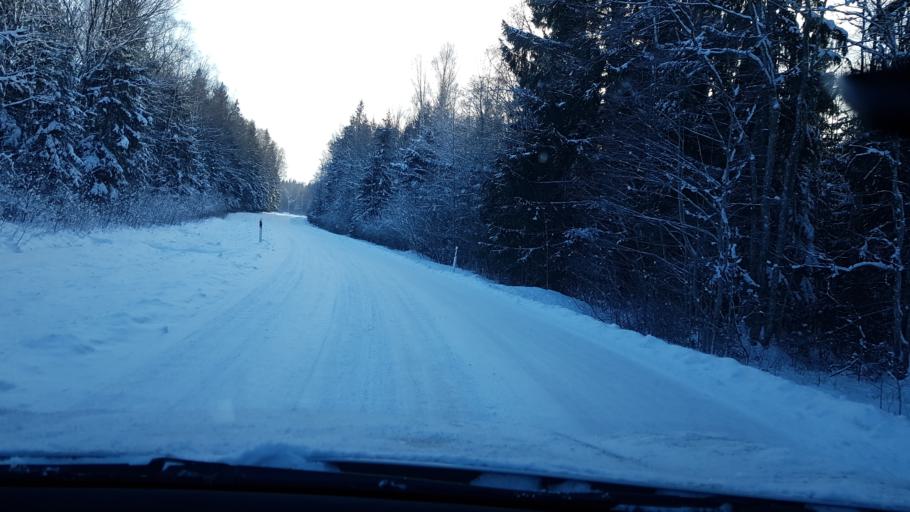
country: EE
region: Harju
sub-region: Nissi vald
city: Turba
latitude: 59.1317
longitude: 24.1958
